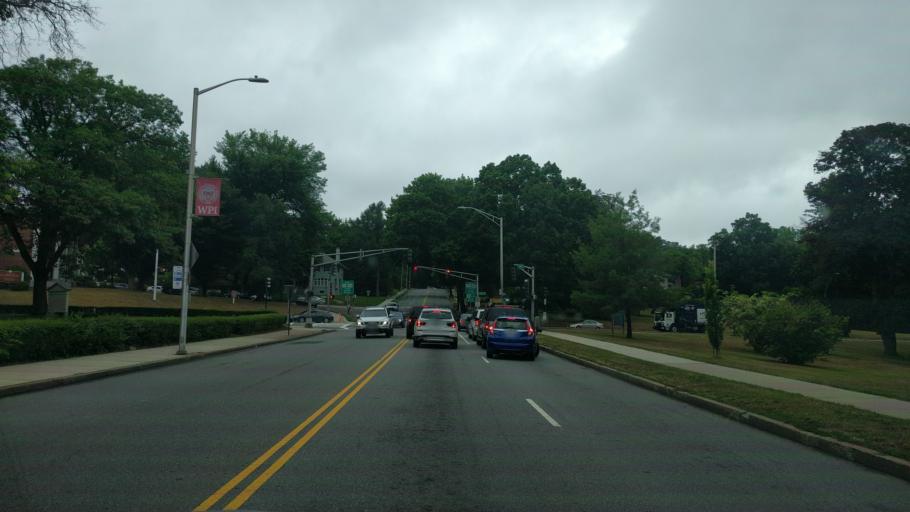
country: US
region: Massachusetts
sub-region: Worcester County
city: Worcester
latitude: 42.2771
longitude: -71.8087
